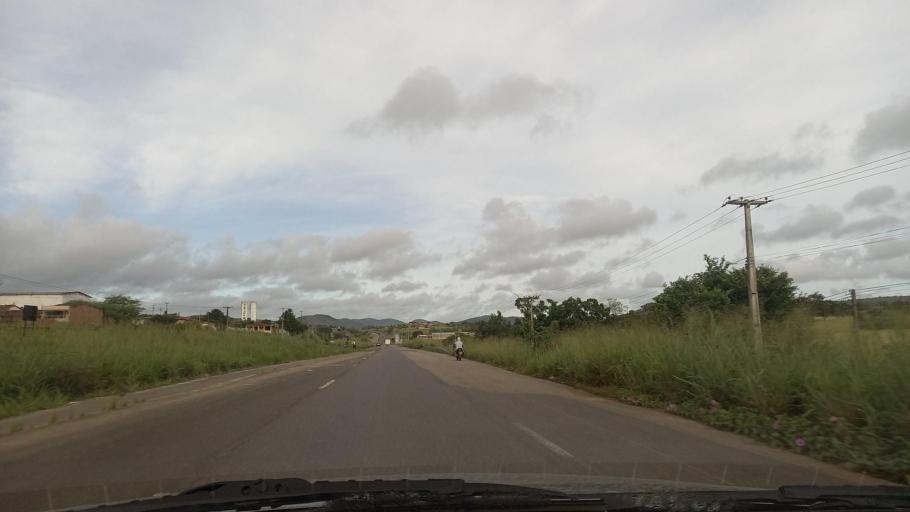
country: BR
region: Pernambuco
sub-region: Pombos
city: Pombos
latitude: -8.1279
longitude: -35.3537
